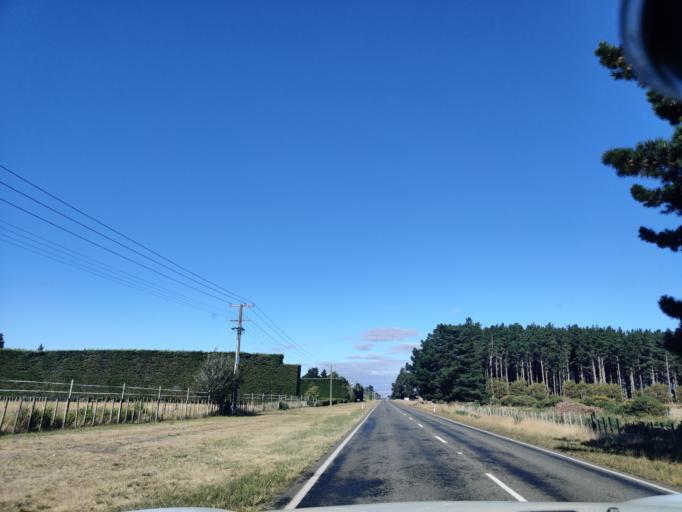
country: NZ
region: Manawatu-Wanganui
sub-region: Horowhenua District
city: Foxton
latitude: -40.3973
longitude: 175.3436
